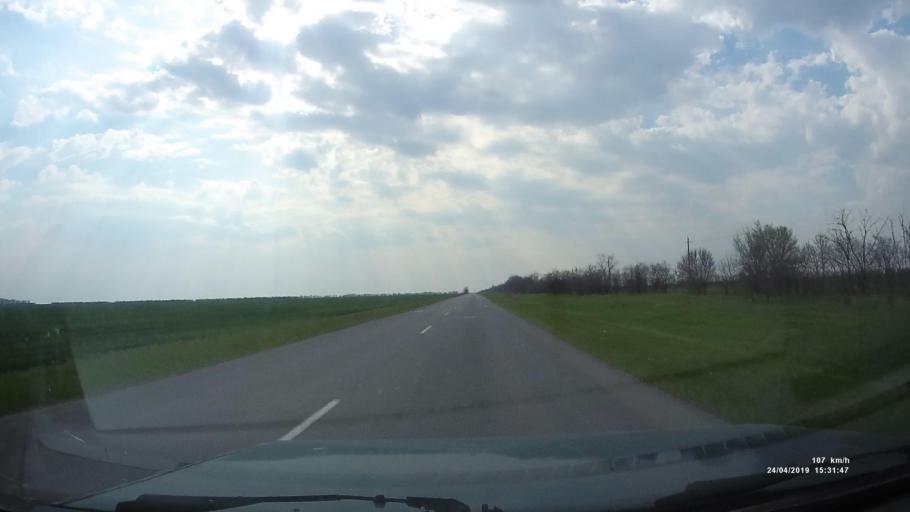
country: RU
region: Rostov
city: Remontnoye
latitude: 46.5996
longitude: 42.9757
